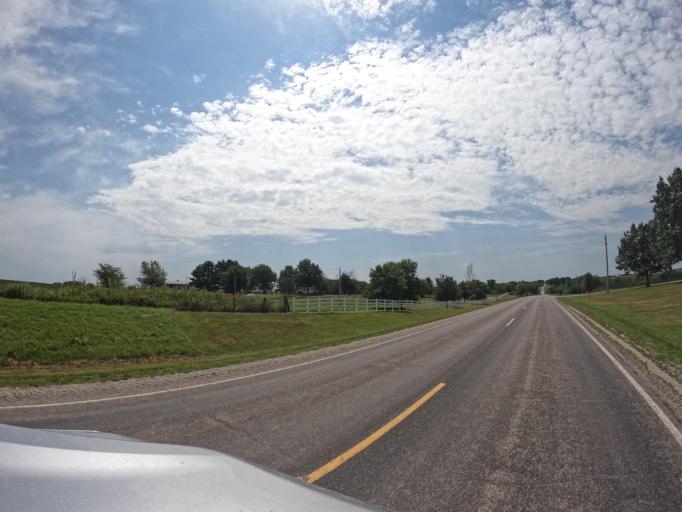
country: US
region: Iowa
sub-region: Appanoose County
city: Centerville
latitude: 40.8023
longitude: -92.9448
